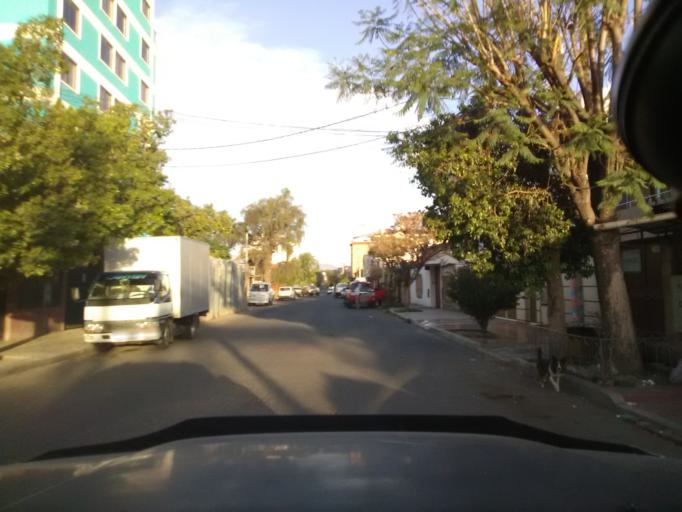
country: BO
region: Cochabamba
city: Cochabamba
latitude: -17.3770
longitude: -66.1776
